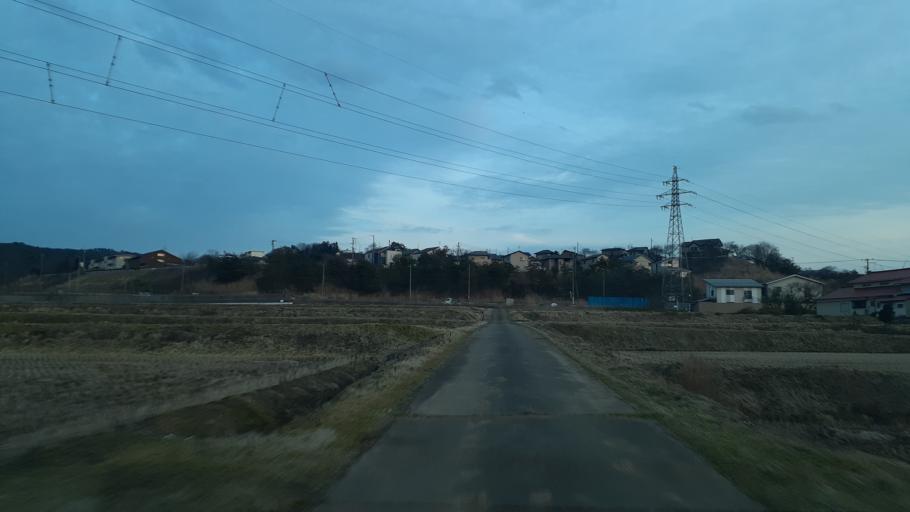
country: JP
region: Fukushima
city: Kitakata
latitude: 37.5352
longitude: 139.9518
